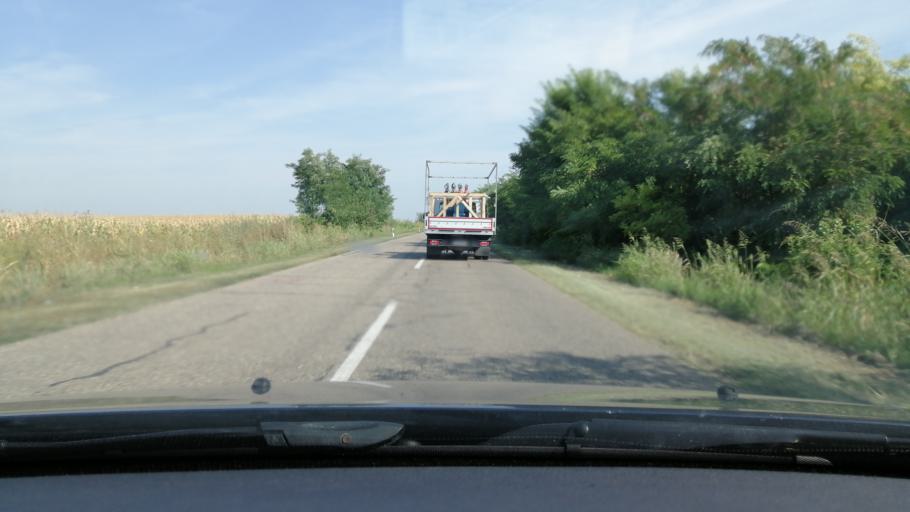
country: RS
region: Autonomna Pokrajina Vojvodina
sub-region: Juznobanatski Okrug
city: Kovacica
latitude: 45.1304
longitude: 20.6161
